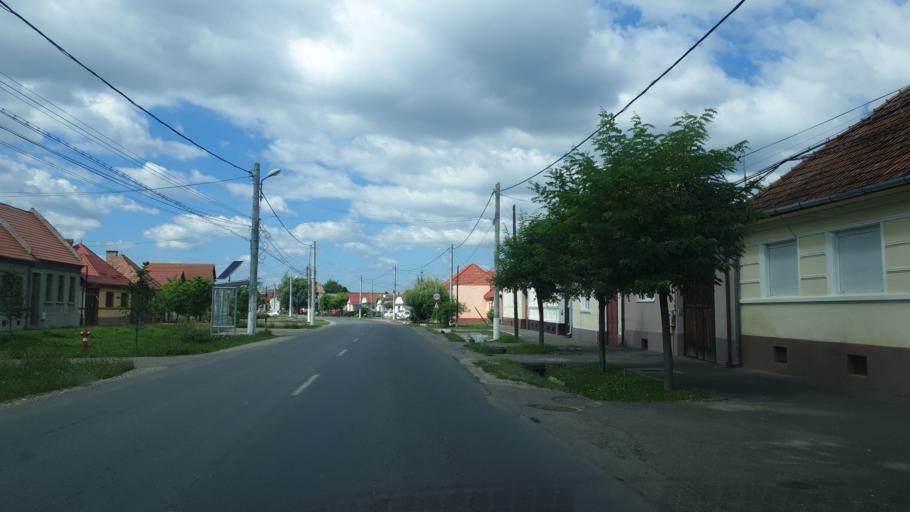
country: RO
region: Brasov
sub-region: Comuna Sanpetru
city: Sanpetru
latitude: 45.7152
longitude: 25.6305
